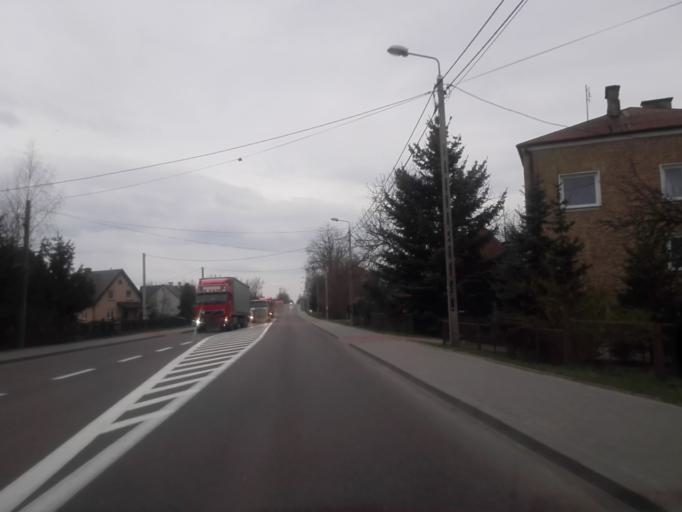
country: PL
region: Podlasie
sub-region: Powiat grajewski
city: Rajgrod
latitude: 53.7712
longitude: 22.8178
